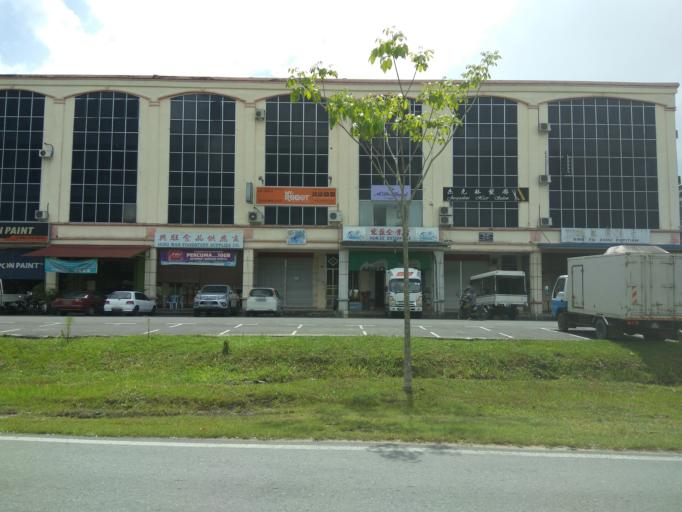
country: MY
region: Sarawak
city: Sibu
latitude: 2.2762
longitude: 111.8537
